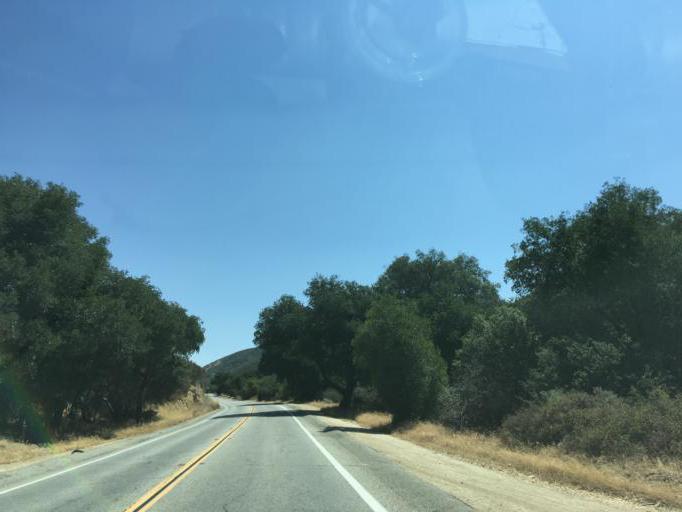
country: US
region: California
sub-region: Los Angeles County
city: Green Valley
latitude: 34.6307
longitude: -118.3968
